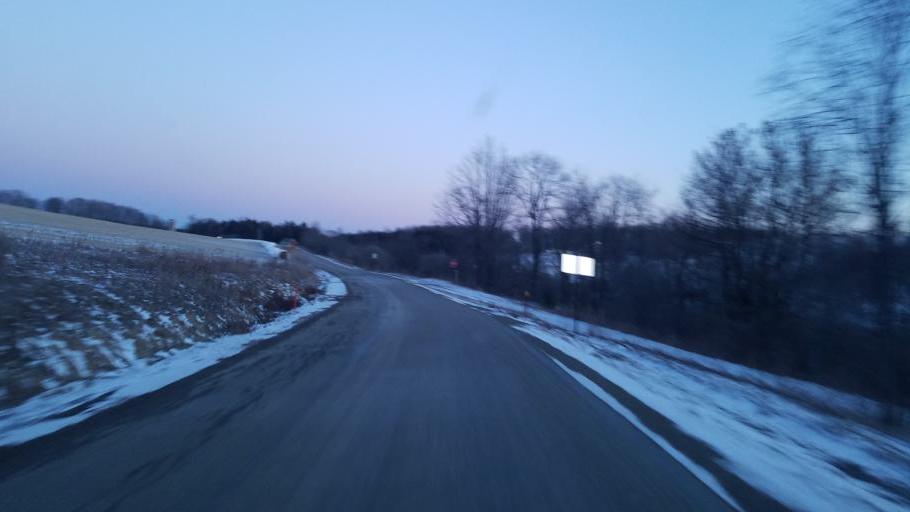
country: US
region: New York
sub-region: Allegany County
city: Andover
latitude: 41.9971
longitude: -77.7694
